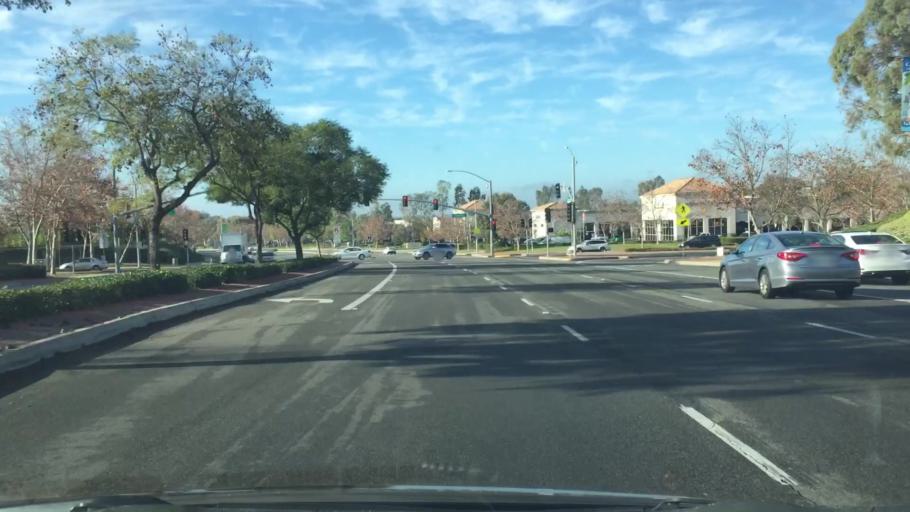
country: US
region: California
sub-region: Orange County
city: Rancho Santa Margarita
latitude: 33.6285
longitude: -117.6034
